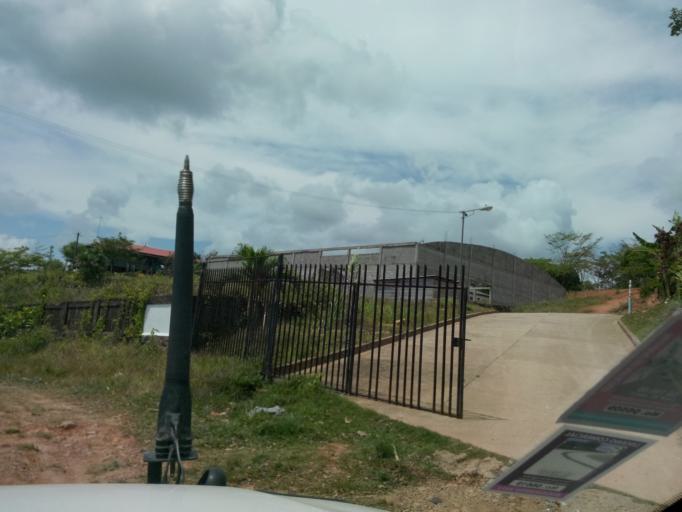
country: NI
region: Atlantico Sur
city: Bluefields
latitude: 12.0113
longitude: -83.7748
